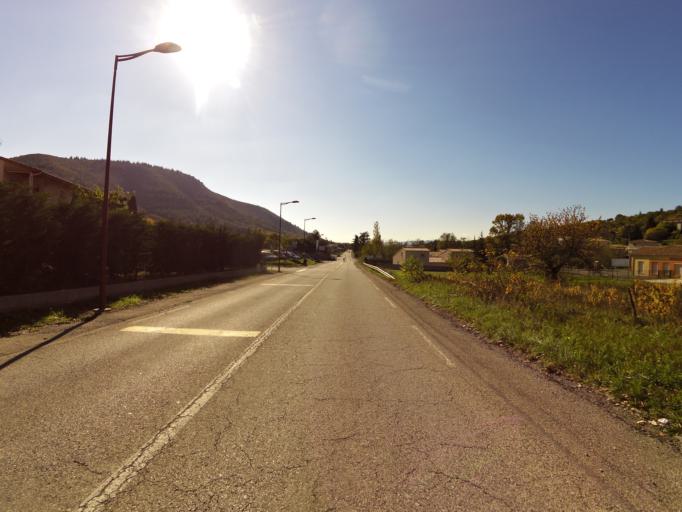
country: FR
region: Rhone-Alpes
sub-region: Departement de l'Ardeche
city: Vesseaux
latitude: 44.6501
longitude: 4.4414
